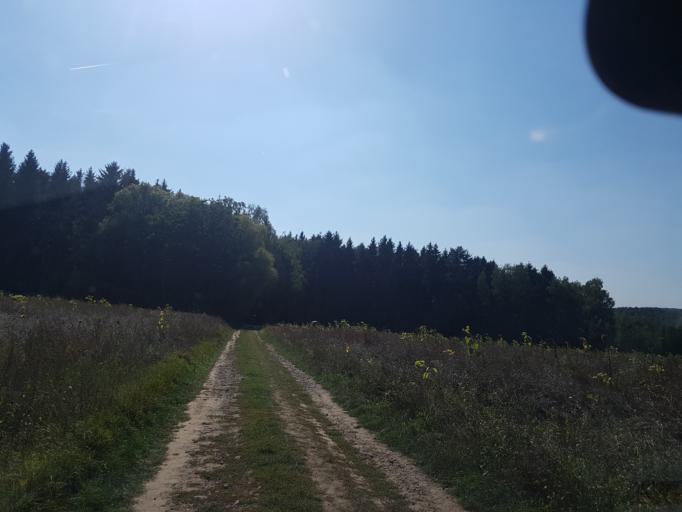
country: DE
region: Saxony
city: Kriebstein
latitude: 51.0563
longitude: 13.0093
